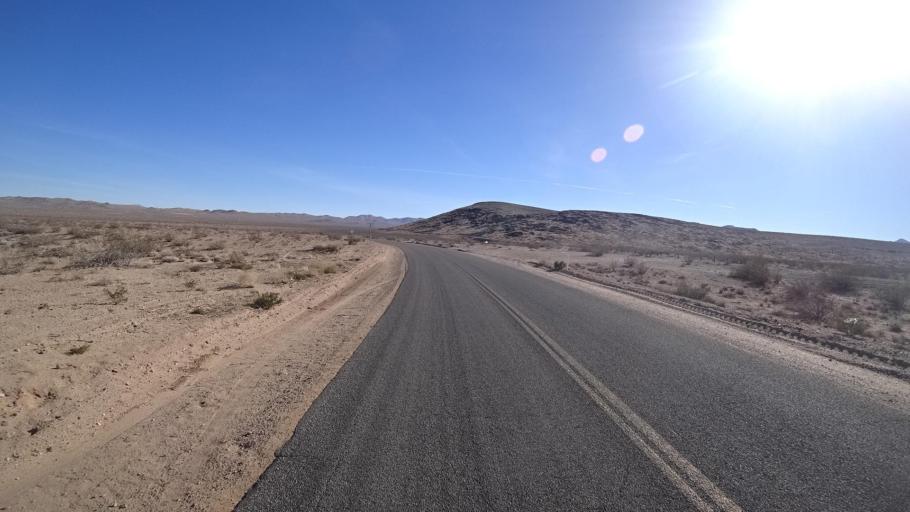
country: US
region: California
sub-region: Kern County
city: China Lake Acres
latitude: 35.5641
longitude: -117.7766
